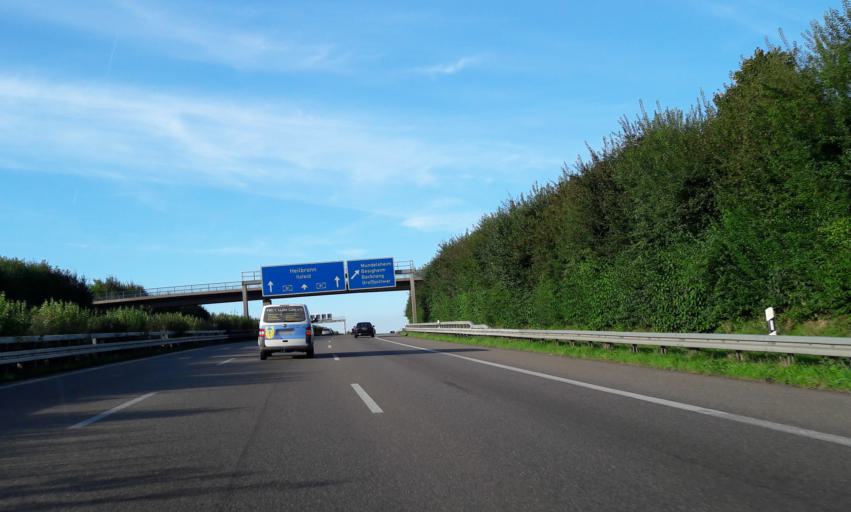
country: DE
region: Baden-Wuerttemberg
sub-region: Regierungsbezirk Stuttgart
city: Mundelsheim
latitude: 49.0008
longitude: 9.2346
